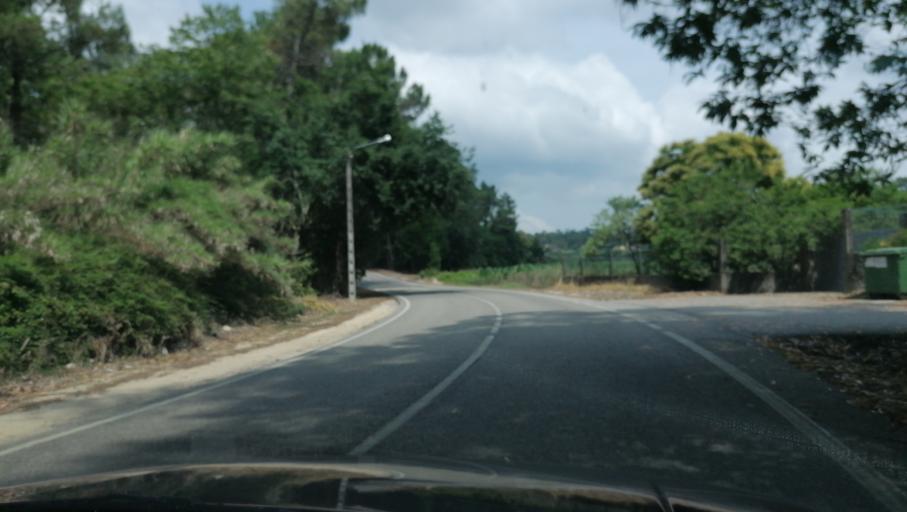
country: ES
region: Galicia
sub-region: Provincia de Pontevedra
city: Tomino
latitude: 42.0067
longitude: -8.7221
